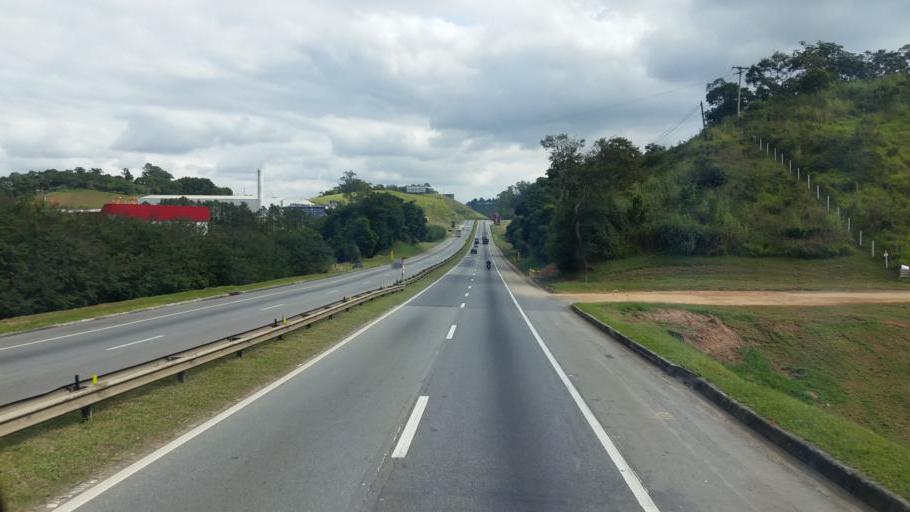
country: BR
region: Sao Paulo
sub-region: Santa Isabel
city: Santa Isabel
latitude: -23.3658
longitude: -46.2284
